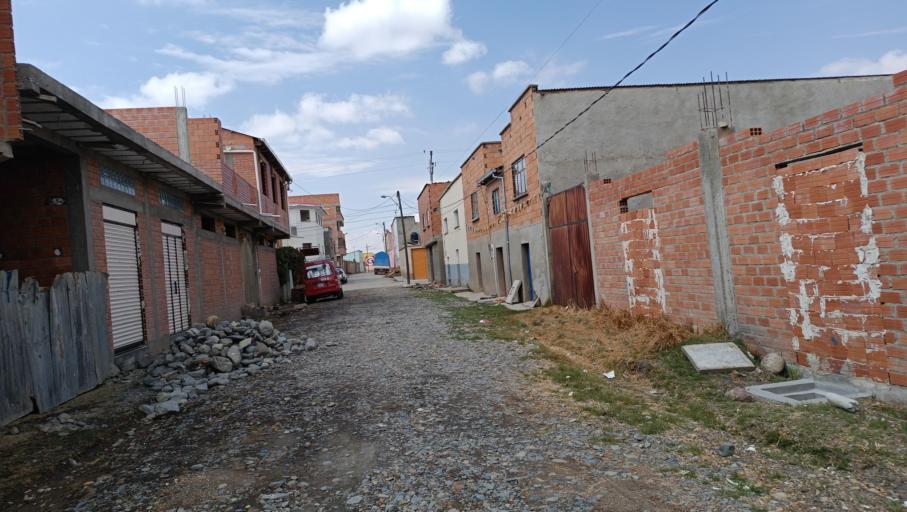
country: BO
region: La Paz
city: Batallas
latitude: -16.3979
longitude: -68.4771
